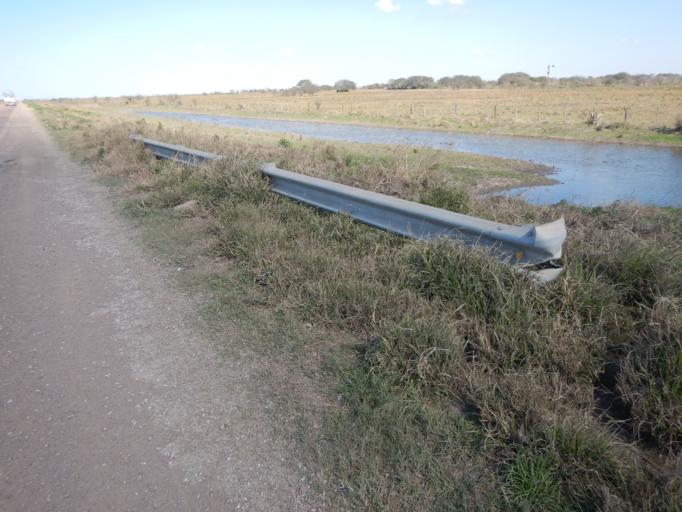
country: AR
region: Santa Fe
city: Tostado
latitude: -28.6772
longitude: -61.5318
